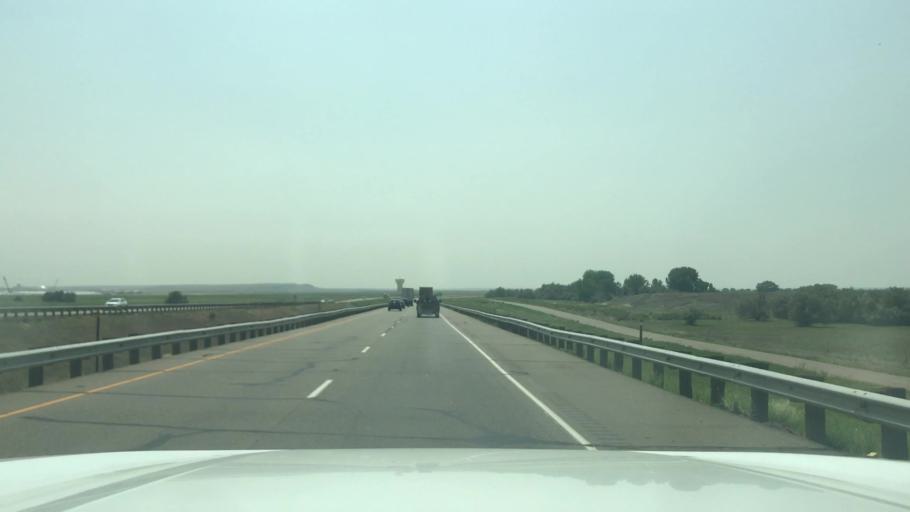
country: US
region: Colorado
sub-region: Pueblo County
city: Pueblo
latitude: 38.1823
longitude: -104.6340
